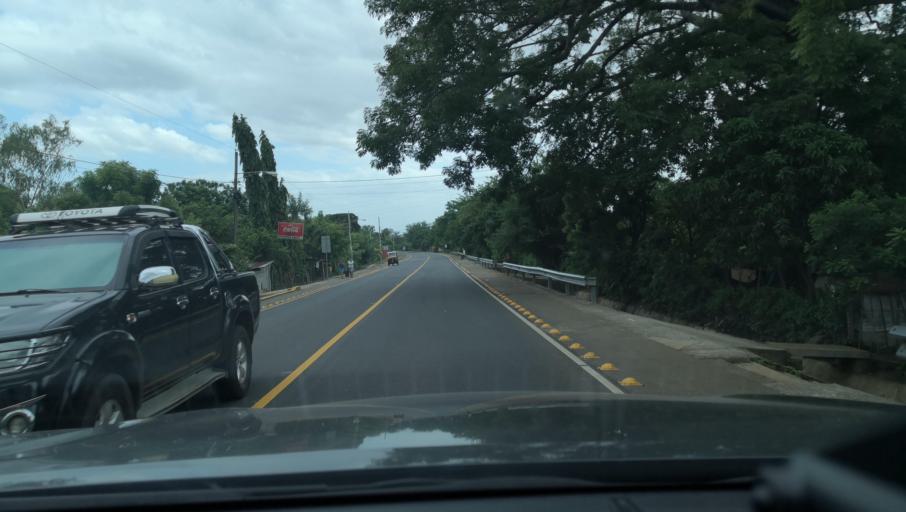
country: NI
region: Masaya
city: Nindiri
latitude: 12.0533
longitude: -86.1353
